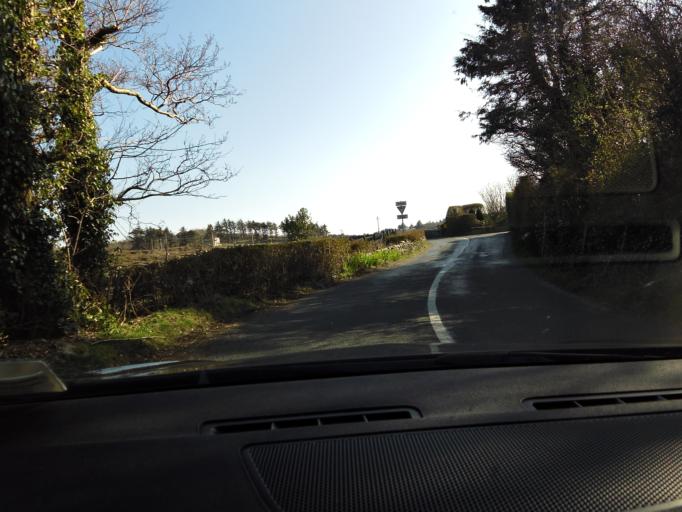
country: IE
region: Connaught
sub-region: County Galway
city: Clifden
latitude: 53.4744
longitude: -10.0195
